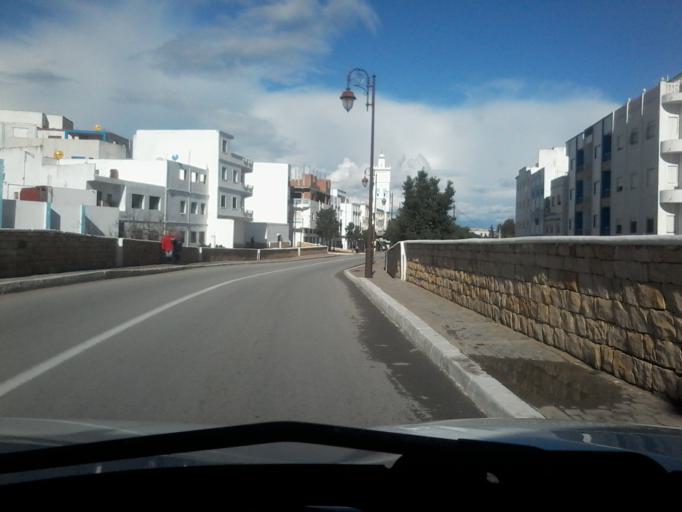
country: MA
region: Tanger-Tetouan
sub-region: Tetouan
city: Martil
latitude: 35.6868
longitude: -5.3309
